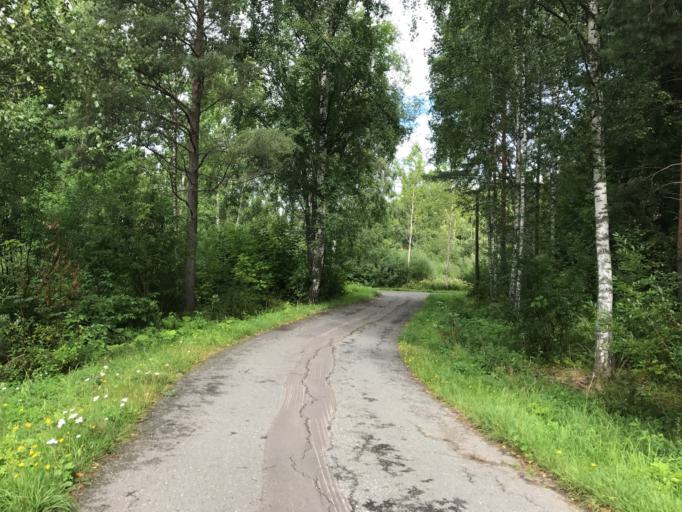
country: FI
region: Pirkanmaa
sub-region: Etelae-Pirkanmaa
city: Valkeakoski
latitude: 61.2557
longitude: 24.0438
